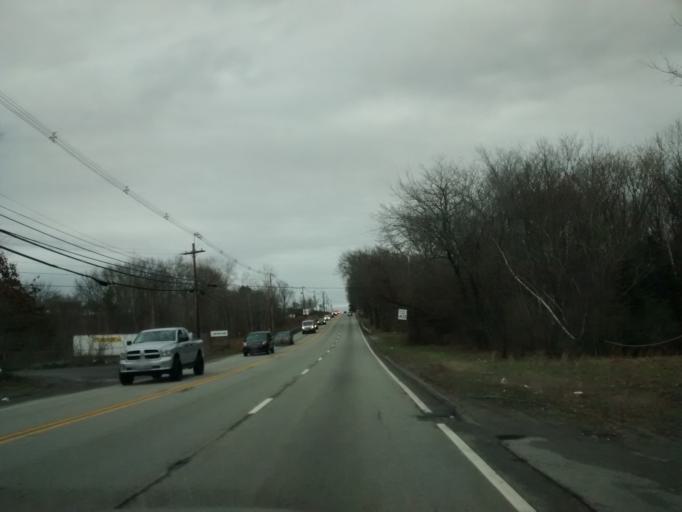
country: US
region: Massachusetts
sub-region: Worcester County
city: Hamilton
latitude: 42.2481
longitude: -71.7241
